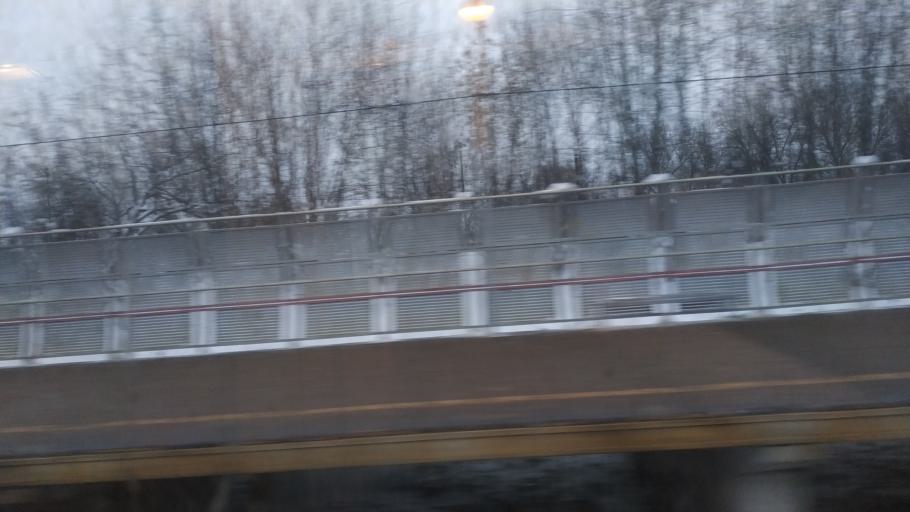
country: RU
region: Moskovskaya
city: Shcherbinka
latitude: 55.4694
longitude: 37.5557
